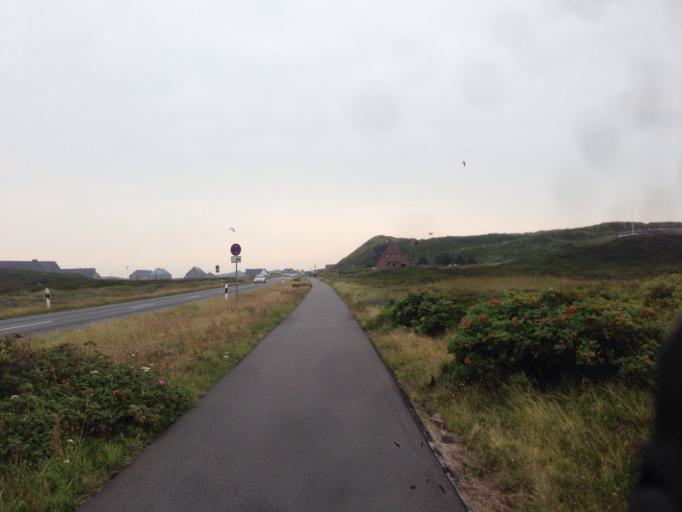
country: DE
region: Schleswig-Holstein
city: Norddorf
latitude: 54.7760
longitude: 8.2846
